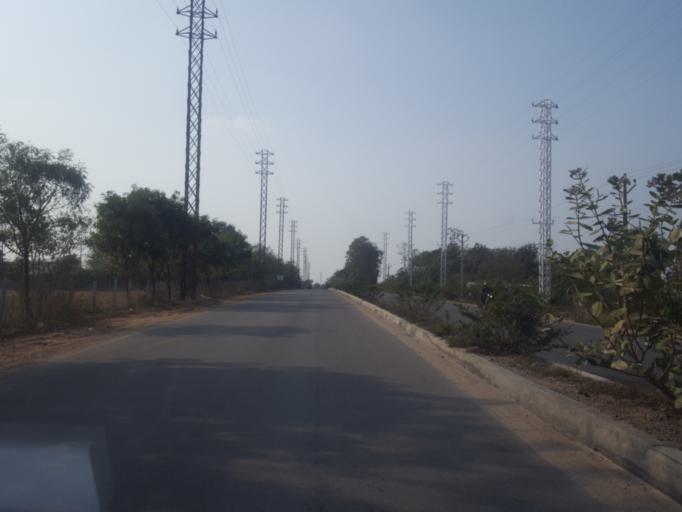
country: IN
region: Telangana
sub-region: Medak
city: Serilingampalle
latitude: 17.4145
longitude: 78.2625
